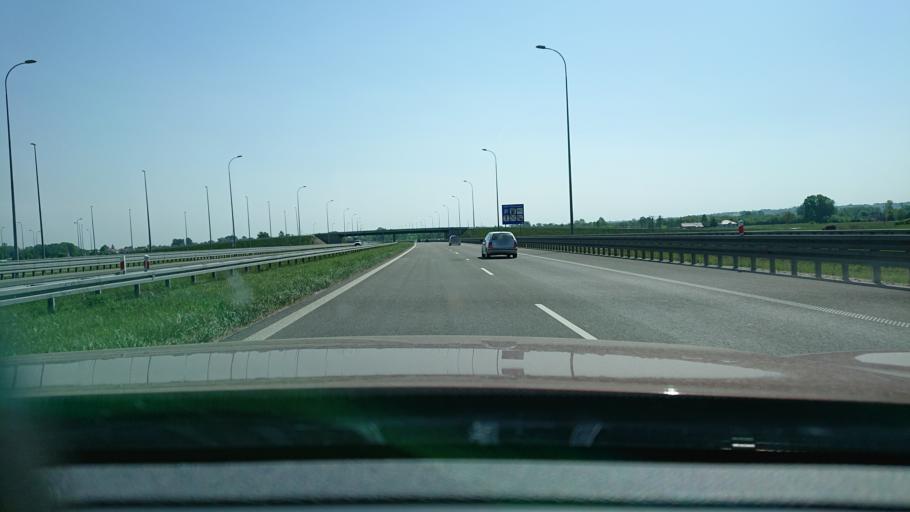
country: PL
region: Subcarpathian Voivodeship
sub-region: Powiat lancucki
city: Czarna
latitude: 50.0903
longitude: 22.1648
